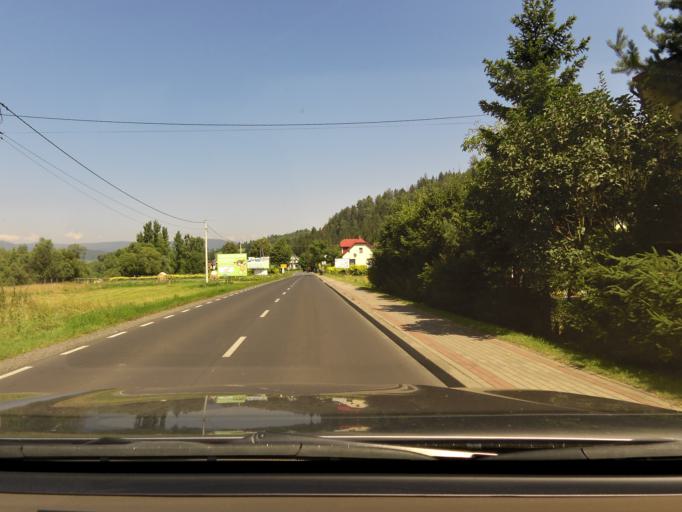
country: PL
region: Silesian Voivodeship
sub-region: Powiat zywiecki
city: Rajcza
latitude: 49.5355
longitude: 19.1103
